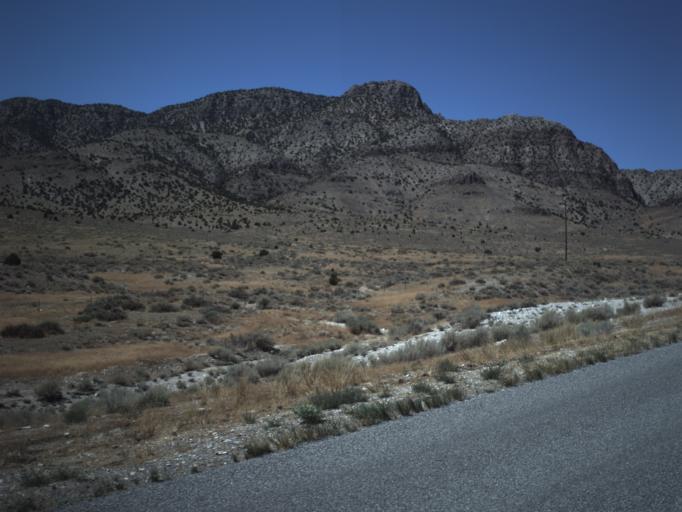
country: US
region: Utah
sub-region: Beaver County
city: Milford
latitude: 39.0871
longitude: -113.5403
